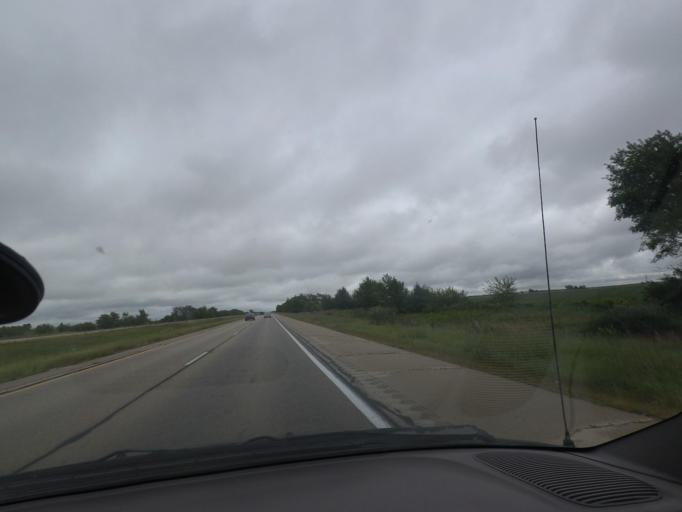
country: US
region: Illinois
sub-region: Piatt County
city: Cerro Gordo
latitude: 40.0192
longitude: -88.7154
